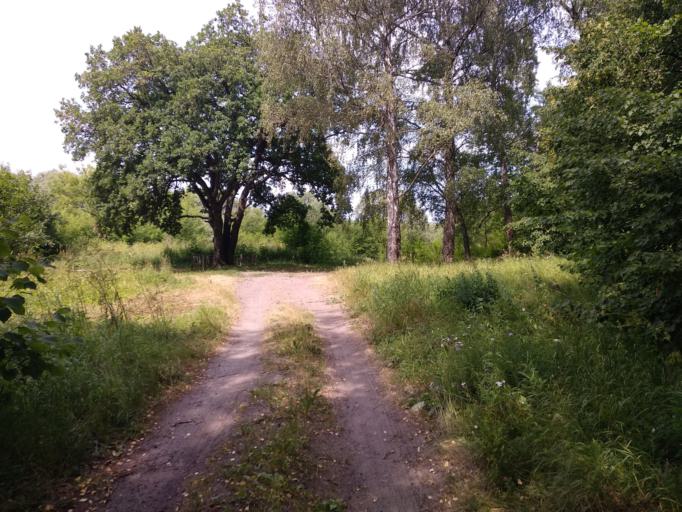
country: RU
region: Moskovskaya
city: Sychevo
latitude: 54.9154
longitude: 38.7481
